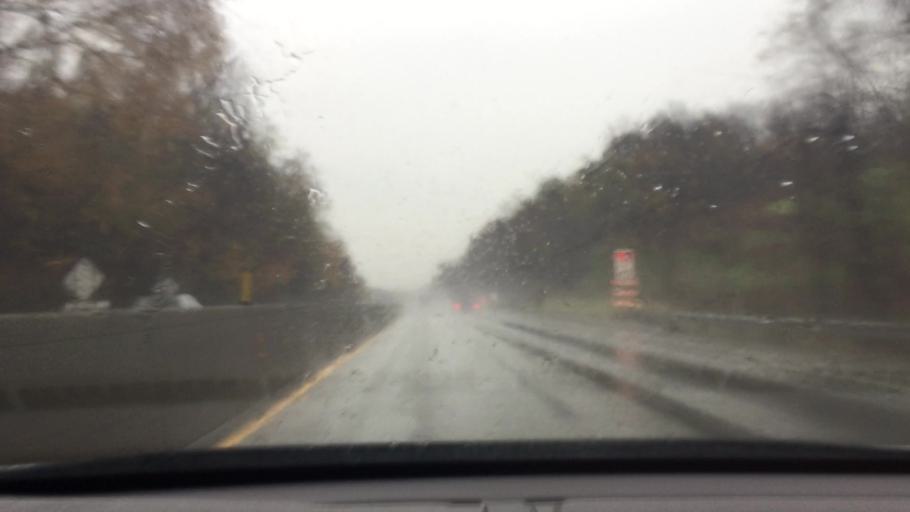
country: US
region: Pennsylvania
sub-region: Washington County
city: East Washington
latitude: 40.1625
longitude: -80.1618
